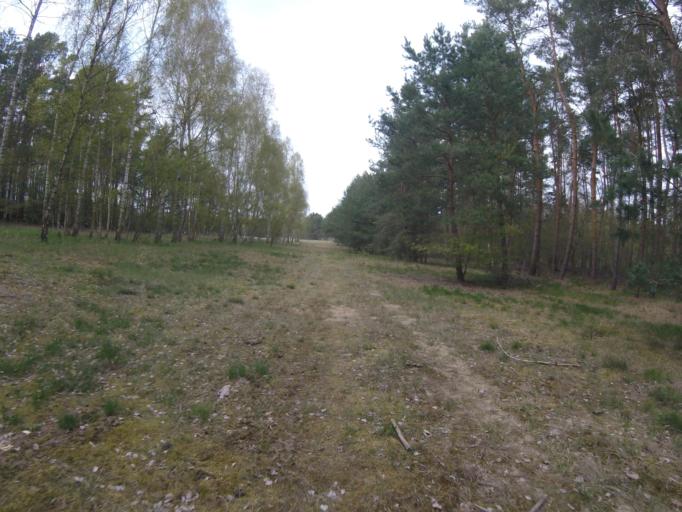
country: DE
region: Brandenburg
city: Bestensee
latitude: 52.2179
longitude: 13.6069
